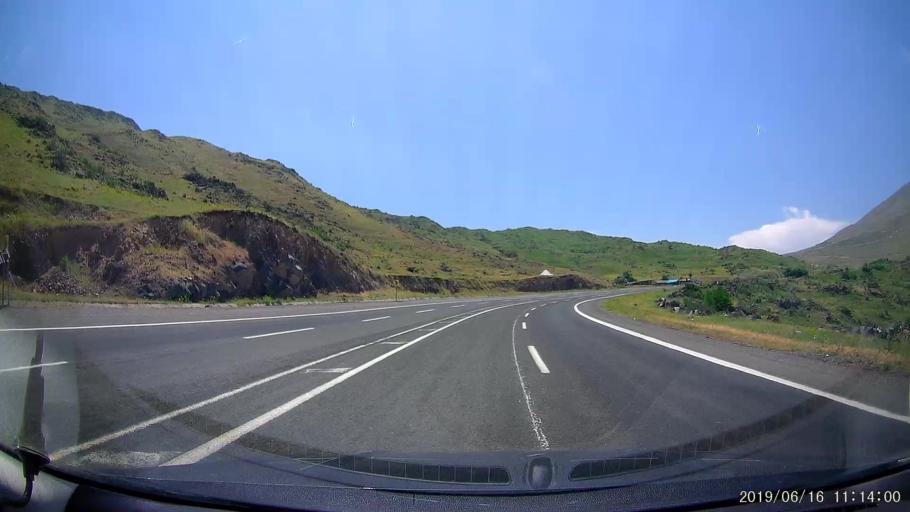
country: TR
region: Igdir
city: Igdir
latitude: 39.7852
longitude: 44.1465
